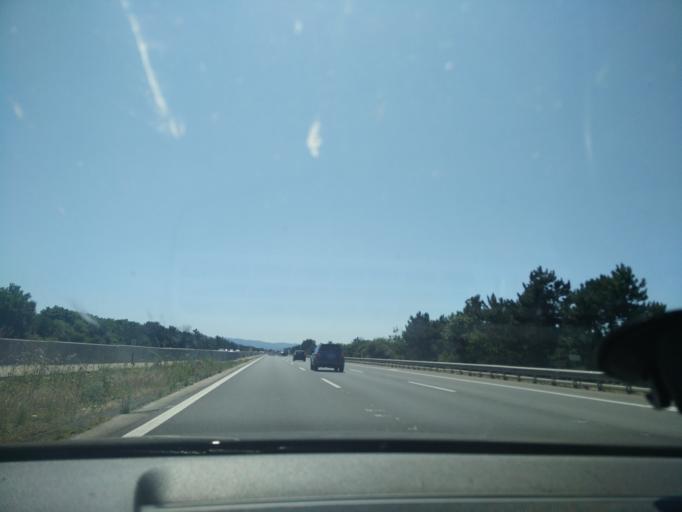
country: AT
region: Lower Austria
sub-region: Politischer Bezirk Wiener Neustadt
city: Weikersdorf am Steinfelde
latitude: 47.8168
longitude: 16.1918
